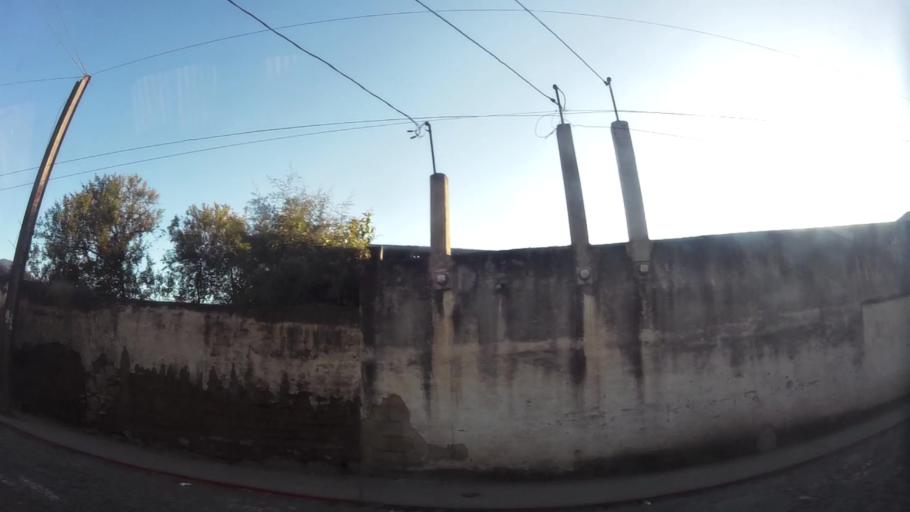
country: GT
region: Sacatepequez
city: Antigua Guatemala
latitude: 14.5626
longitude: -90.7336
